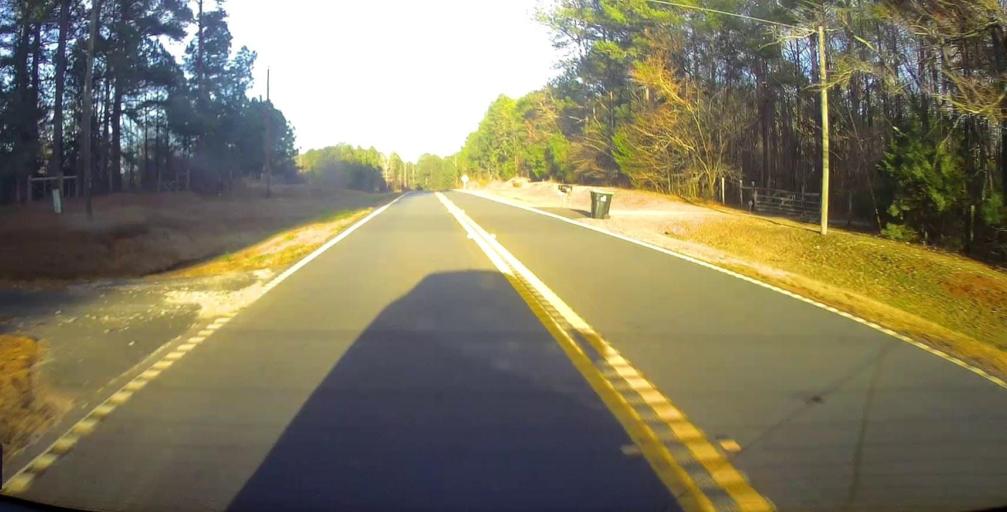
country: US
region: Georgia
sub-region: Talbot County
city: Sardis
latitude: 32.7491
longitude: -84.5808
